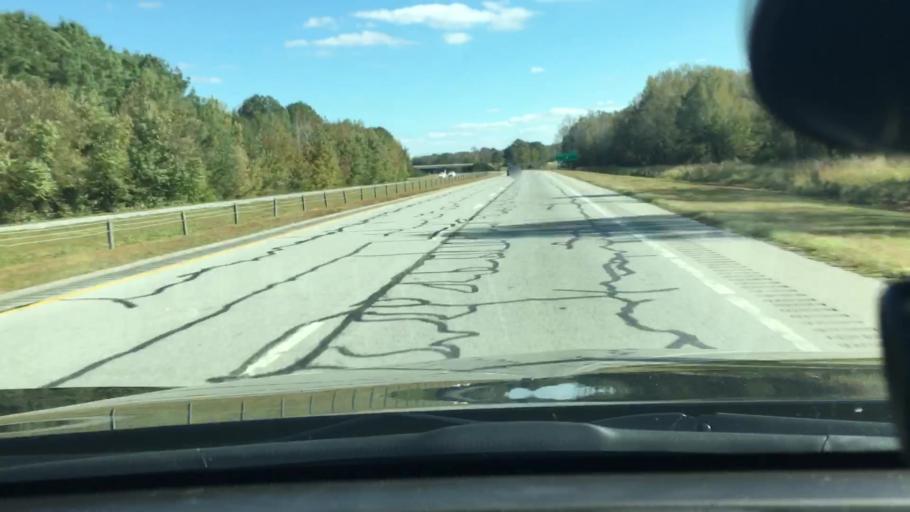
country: US
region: North Carolina
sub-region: Pitt County
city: Farmville
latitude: 35.6028
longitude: -77.5645
